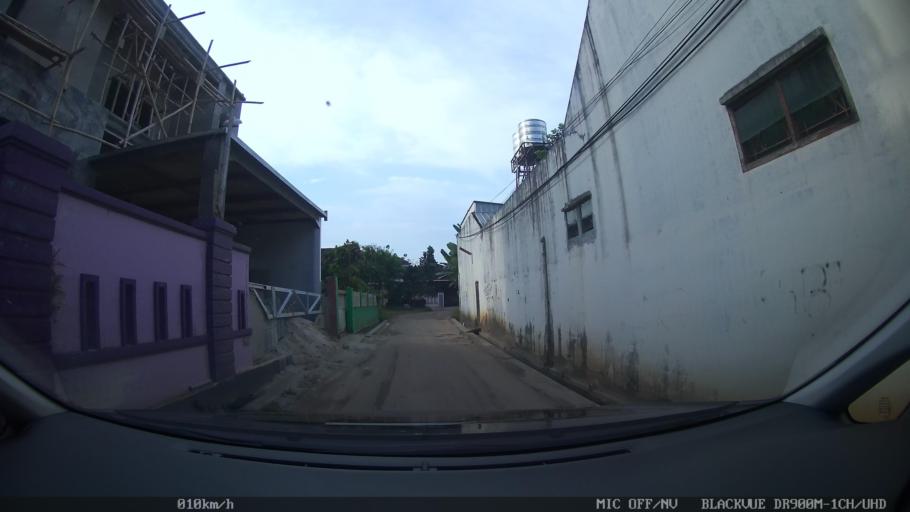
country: ID
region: Lampung
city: Kedaton
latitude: -5.3791
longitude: 105.2387
